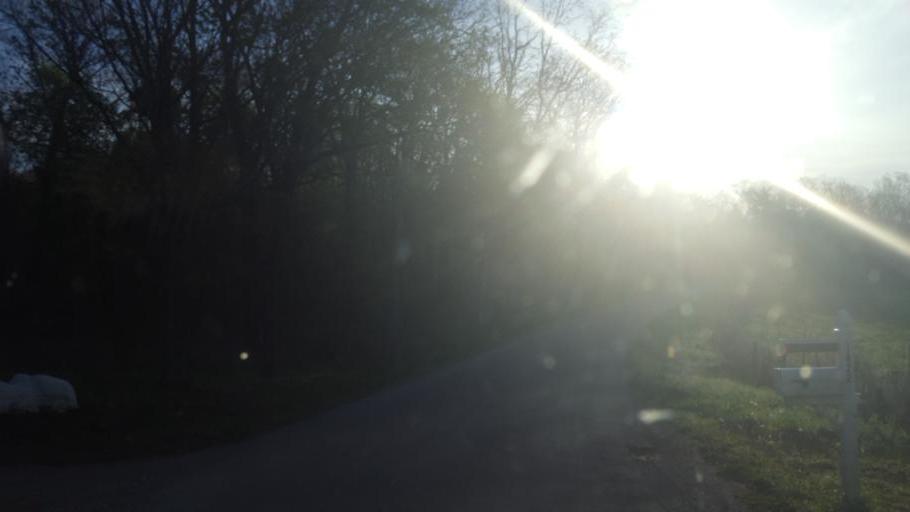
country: US
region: Kentucky
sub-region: Hart County
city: Munfordville
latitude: 37.2445
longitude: -85.9207
